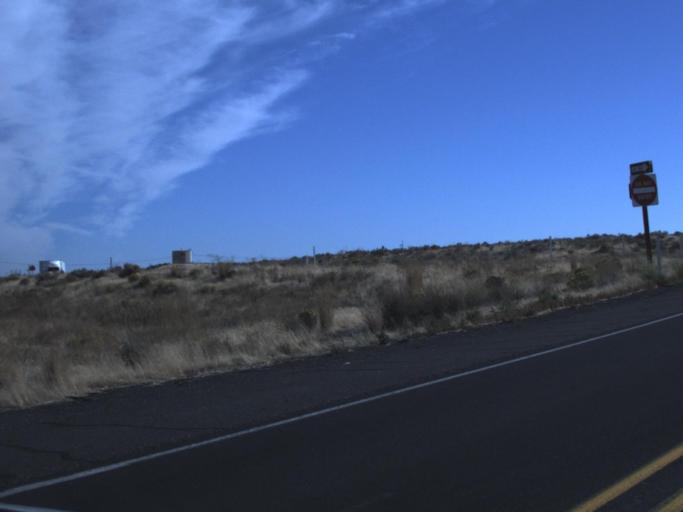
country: US
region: Washington
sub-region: Franklin County
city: Basin City
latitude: 46.5676
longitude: -118.9950
